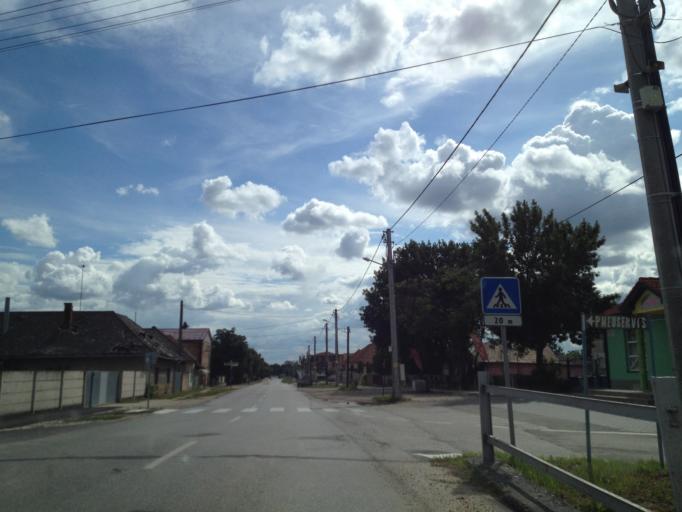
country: SK
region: Nitriansky
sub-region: Okres Komarno
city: Hurbanovo
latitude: 47.8431
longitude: 18.2592
